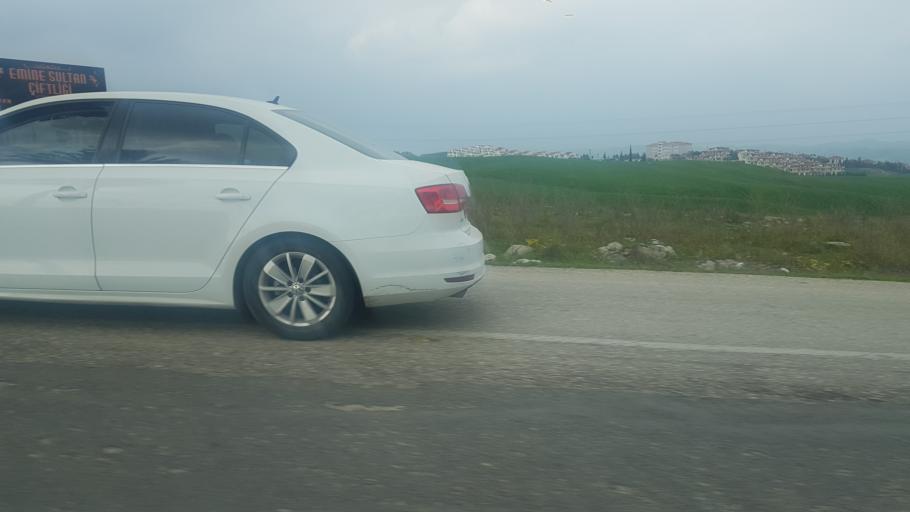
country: TR
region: Adana
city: Seyhan
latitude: 37.0587
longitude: 35.2330
